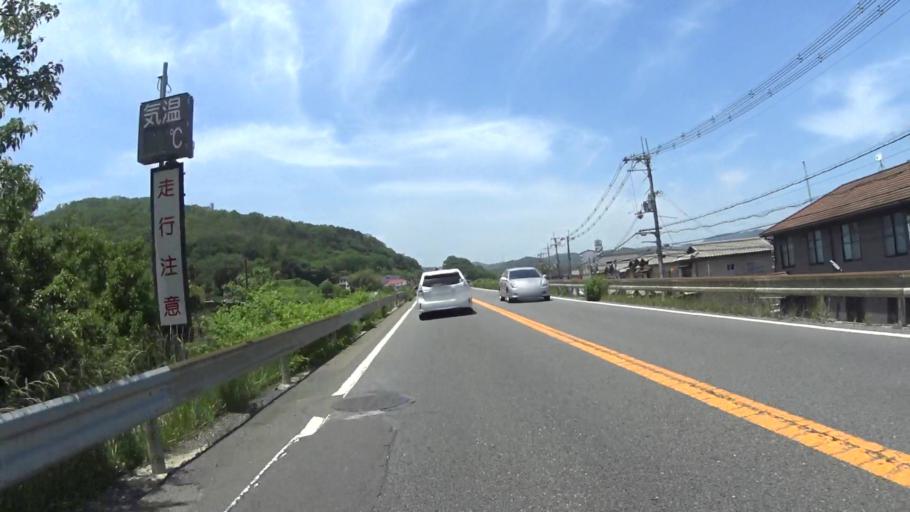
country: JP
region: Kyoto
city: Kameoka
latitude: 35.1044
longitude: 135.4837
